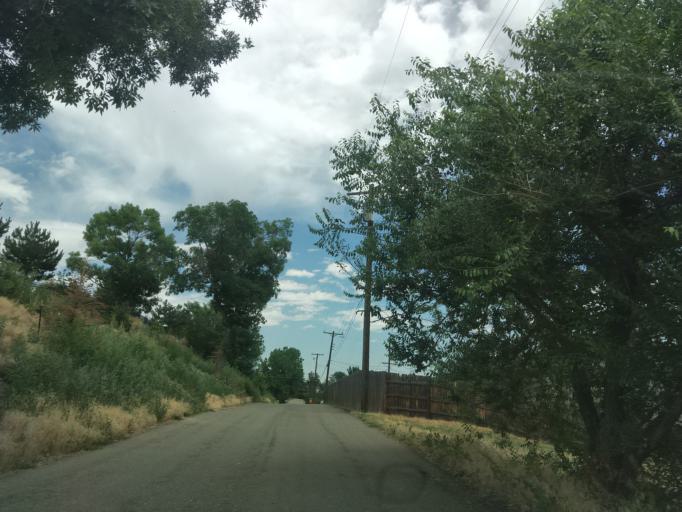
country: US
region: Colorado
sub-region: Jefferson County
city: Lakewood
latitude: 39.6740
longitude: -105.1086
